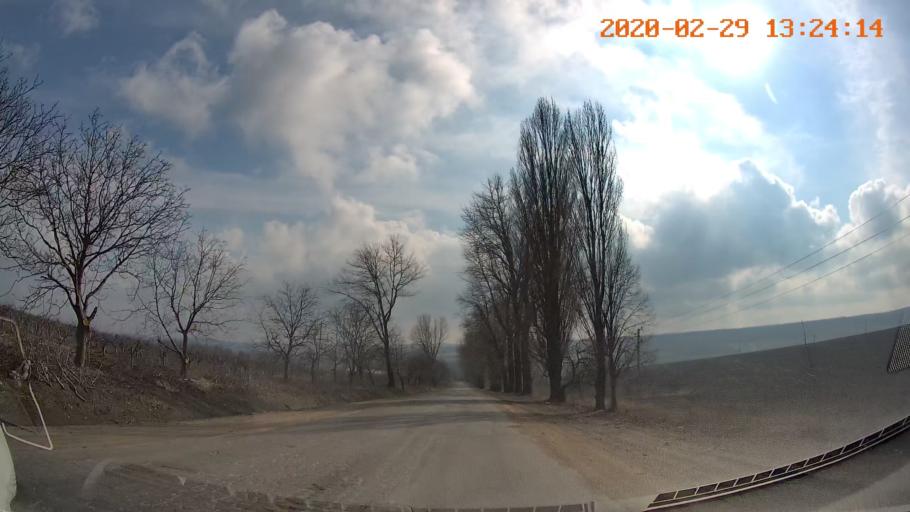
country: MD
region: Telenesti
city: Camenca
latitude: 47.9410
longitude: 28.6265
